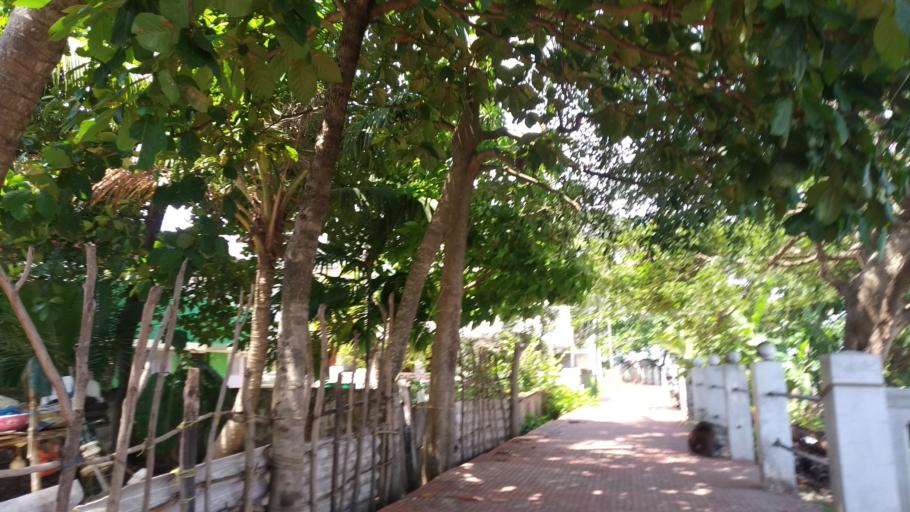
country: IN
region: Kerala
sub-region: Ernakulam
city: Cochin
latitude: 9.9724
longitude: 76.2425
